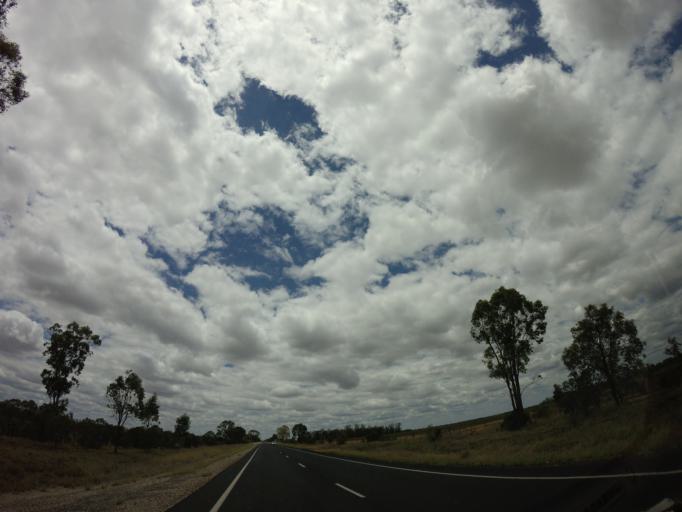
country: AU
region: Queensland
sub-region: Goondiwindi
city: Goondiwindi
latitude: -28.1758
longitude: 150.4818
